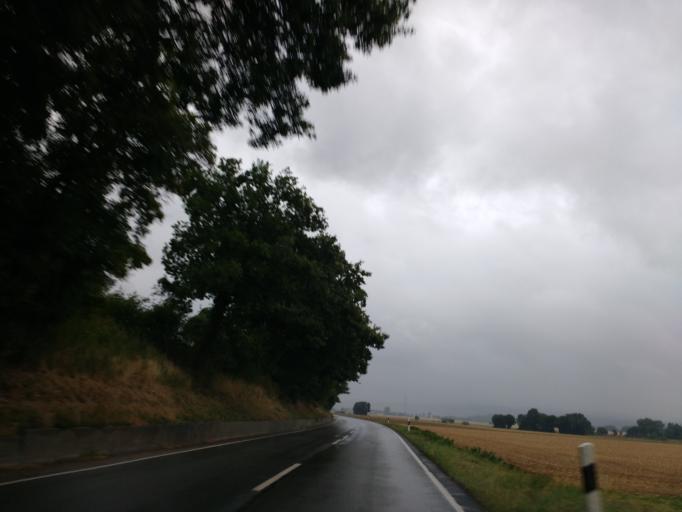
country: DE
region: Lower Saxony
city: Hehlen
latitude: 52.0417
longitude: 9.4198
